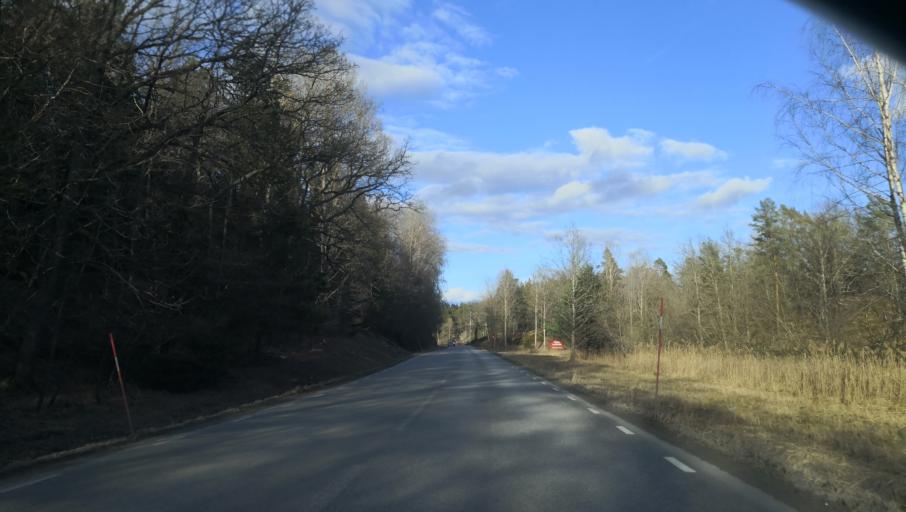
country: SE
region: Stockholm
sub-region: Varmdo Kommun
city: Gustavsberg
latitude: 59.3366
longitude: 18.3499
